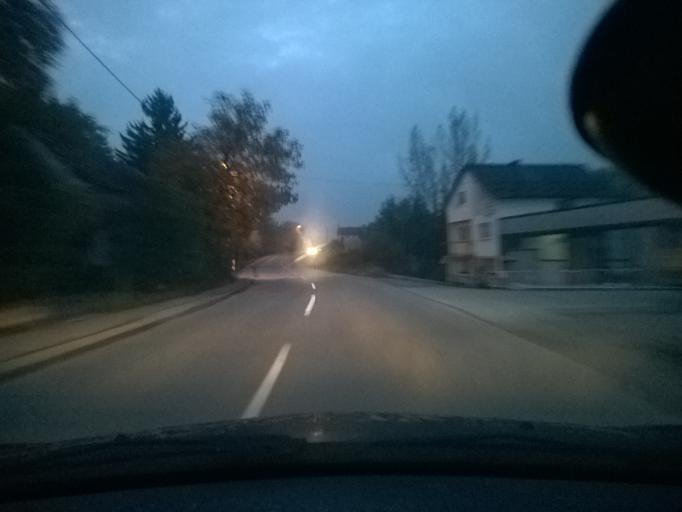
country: HR
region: Krapinsko-Zagorska
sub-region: Grad Krapina
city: Krapina
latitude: 46.1421
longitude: 15.8810
